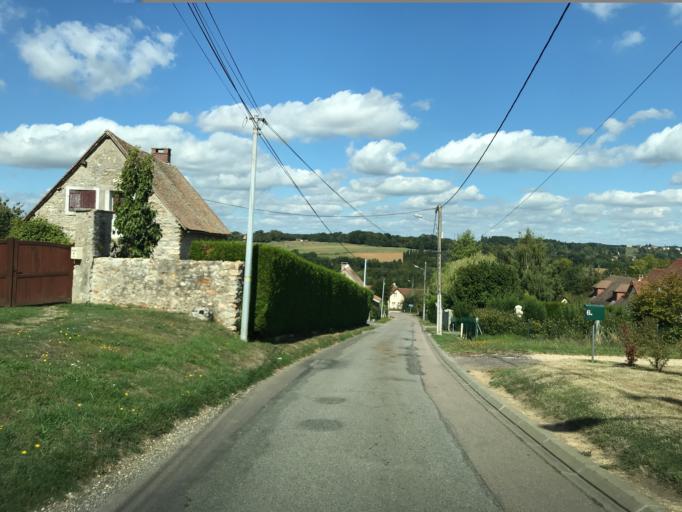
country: FR
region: Haute-Normandie
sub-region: Departement de l'Eure
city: La Chapelle-Reanville
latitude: 49.1066
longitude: 1.3881
